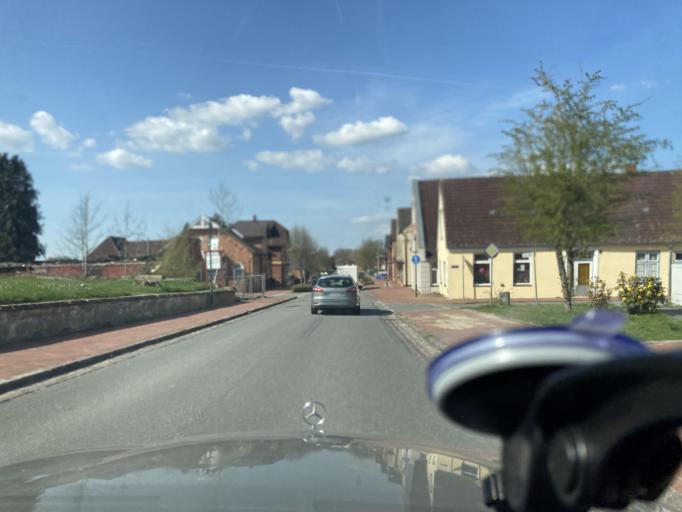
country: DE
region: Schleswig-Holstein
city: Lehe
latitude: 54.3336
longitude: 9.0238
